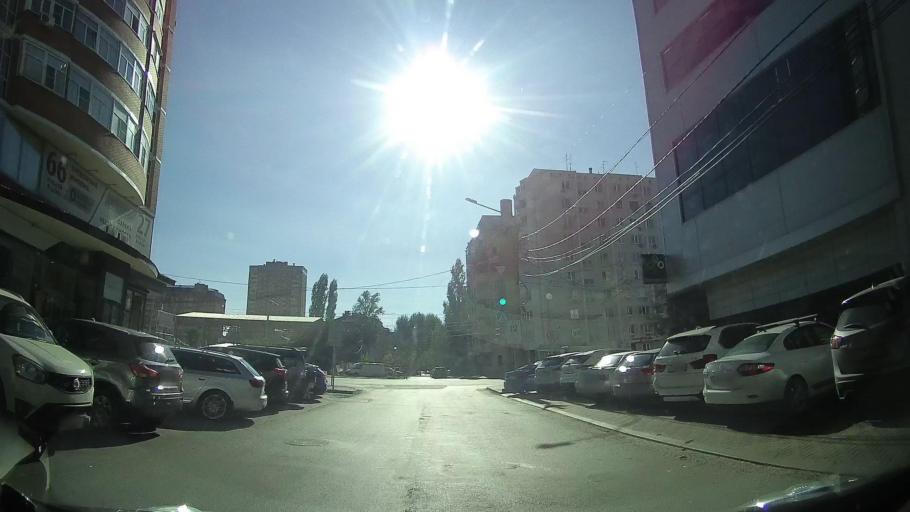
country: RU
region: Rostov
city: Rostov-na-Donu
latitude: 47.2325
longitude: 39.7313
